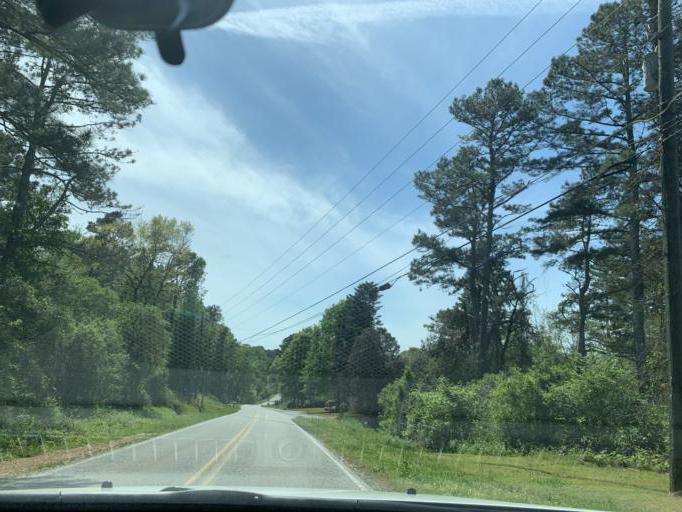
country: US
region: Georgia
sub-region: Forsyth County
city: Cumming
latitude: 34.2729
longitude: -84.1879
